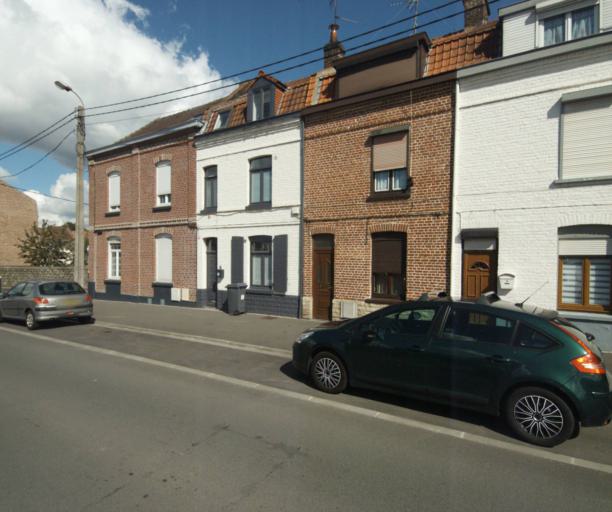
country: FR
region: Nord-Pas-de-Calais
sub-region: Departement du Nord
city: Loos
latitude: 50.6124
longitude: 3.0069
